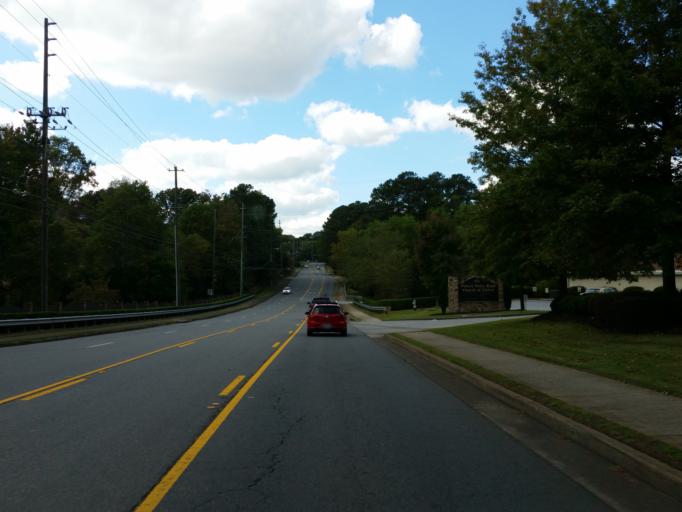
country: US
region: Georgia
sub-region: Cobb County
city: Smyrna
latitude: 33.9308
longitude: -84.4754
